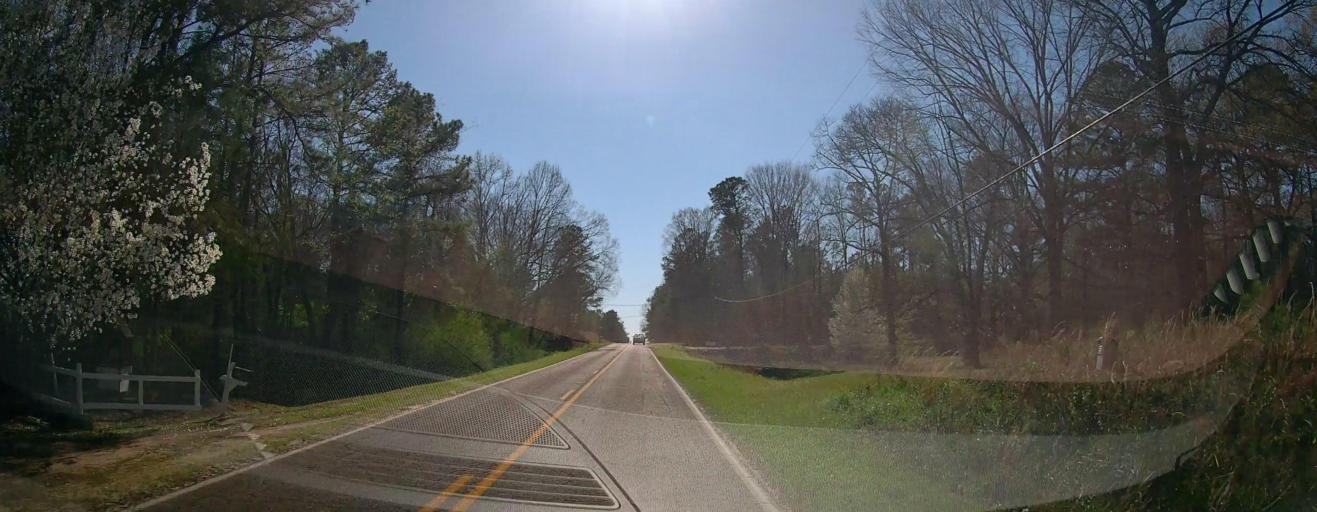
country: US
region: Georgia
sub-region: Peach County
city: Fort Valley
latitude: 32.6520
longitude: -83.8839
